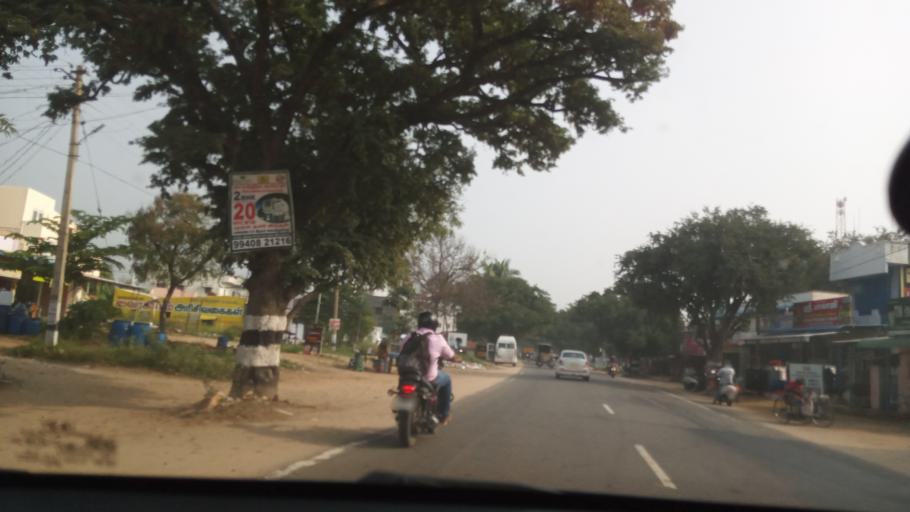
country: IN
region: Tamil Nadu
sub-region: Coimbatore
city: Annur
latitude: 11.1752
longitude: 77.0573
